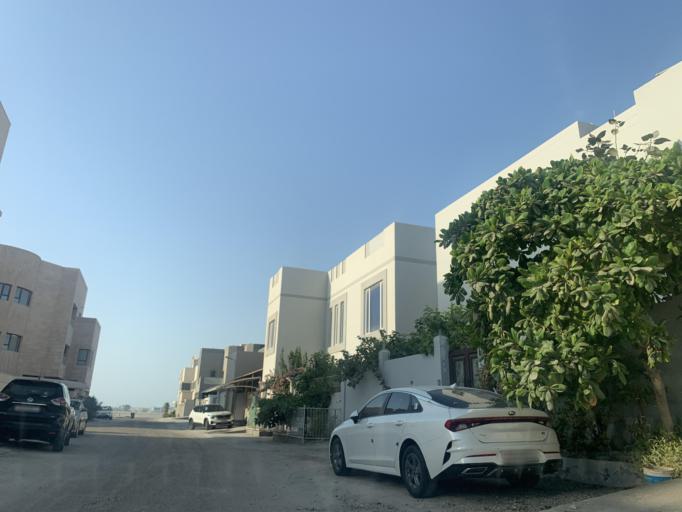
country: BH
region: Muharraq
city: Al Muharraq
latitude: 26.2870
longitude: 50.6317
